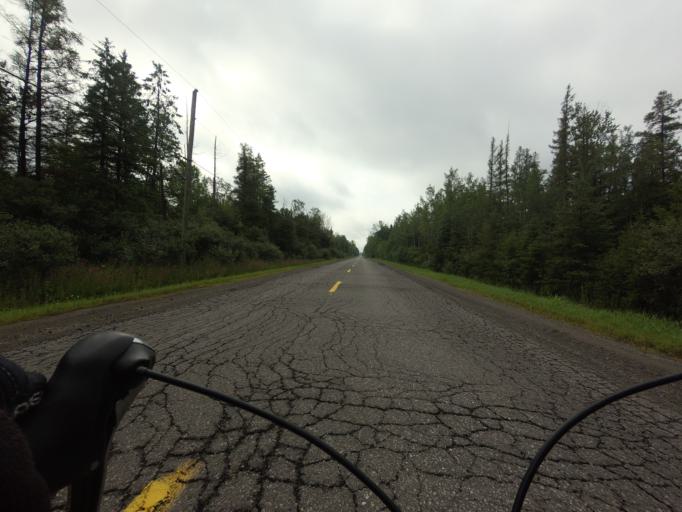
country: CA
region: Ontario
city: Bells Corners
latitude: 45.0643
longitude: -75.7231
